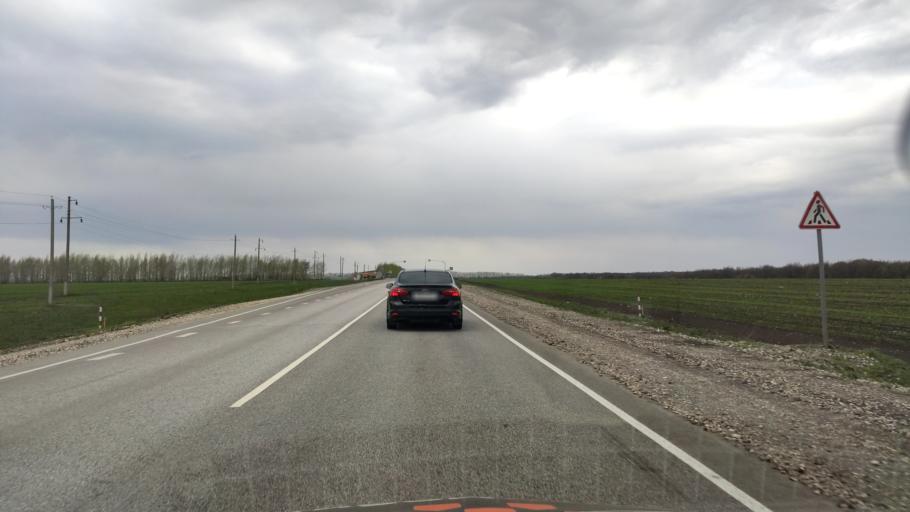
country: RU
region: Voronezj
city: Nizhnedevitsk
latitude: 51.5842
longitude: 38.5456
